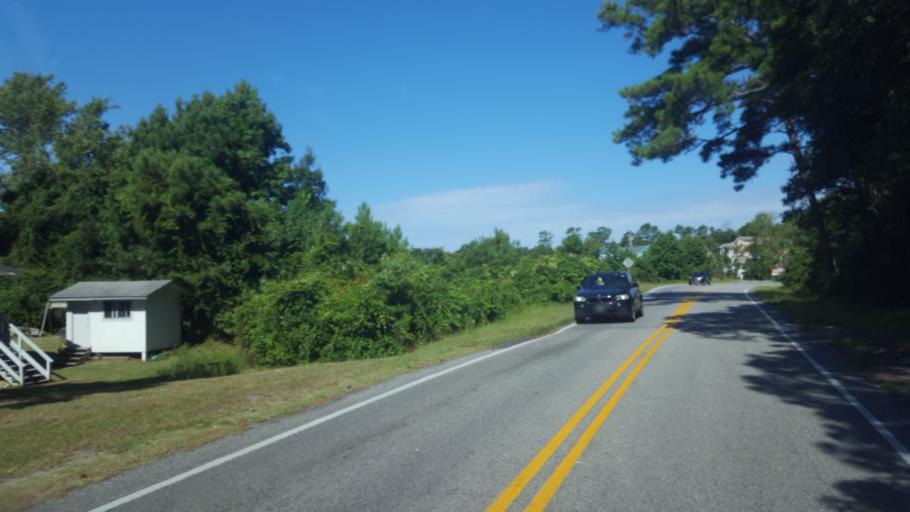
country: US
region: North Carolina
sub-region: Dare County
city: Kill Devil Hills
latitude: 36.0082
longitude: -75.7062
